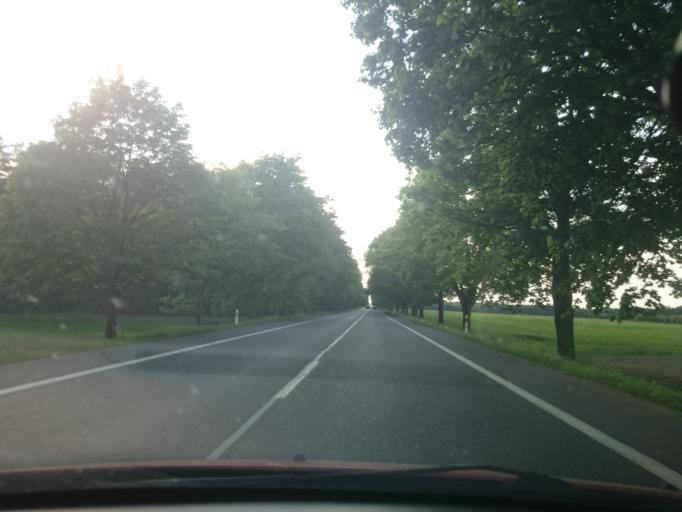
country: PL
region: Opole Voivodeship
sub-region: Powiat strzelecki
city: Strzelce Opolskie
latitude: 50.5426
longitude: 18.2410
